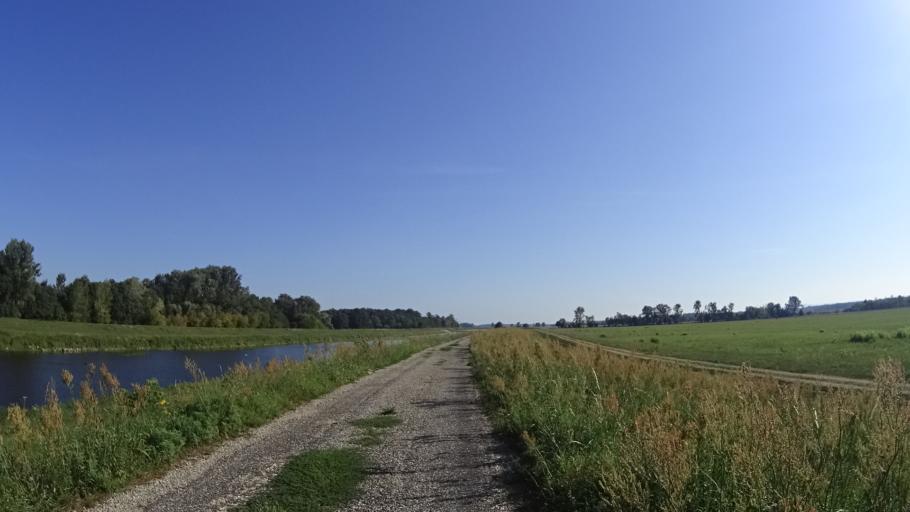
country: CZ
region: South Moravian
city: Tvrdonice
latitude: 48.7296
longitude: 17.0159
